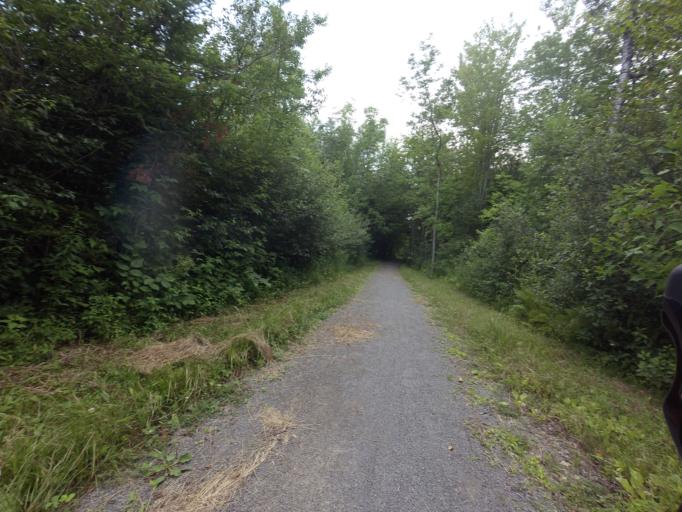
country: CA
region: Ontario
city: Bells Corners
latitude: 45.0325
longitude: -75.6684
